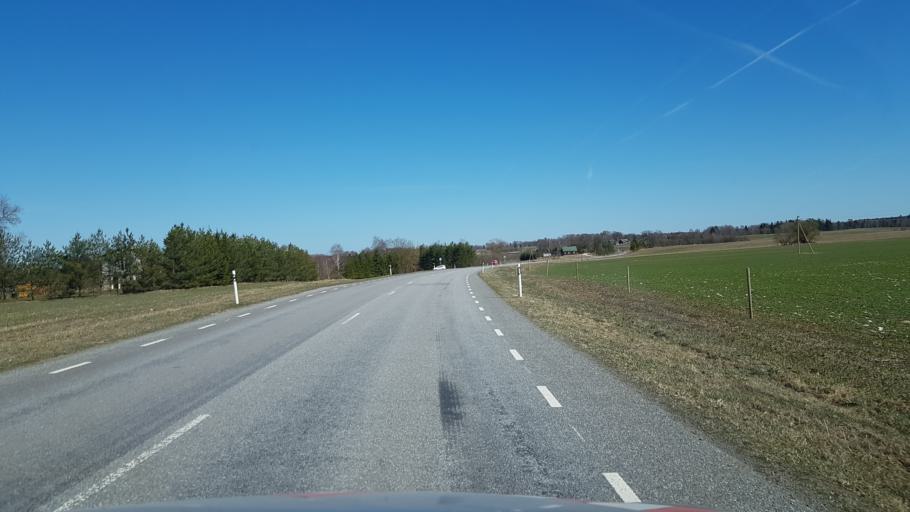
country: EE
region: Laeaene-Virumaa
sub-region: Vinni vald
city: Vinni
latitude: 59.3174
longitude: 26.4694
